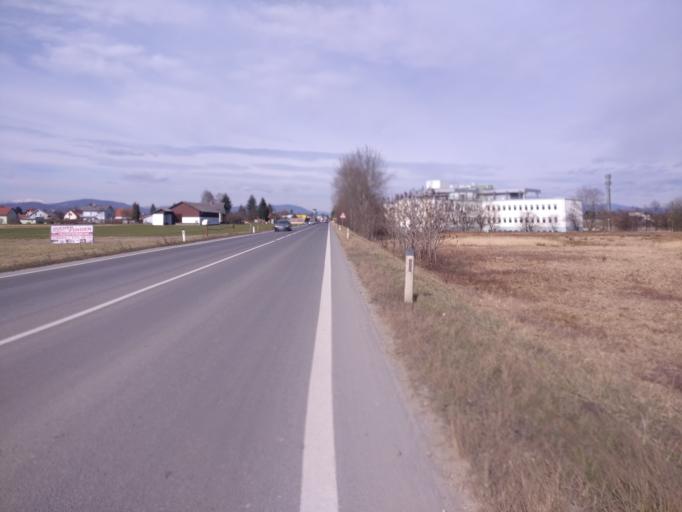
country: AT
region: Styria
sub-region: Politischer Bezirk Graz-Umgebung
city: Gossendorf
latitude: 46.9807
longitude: 15.4542
